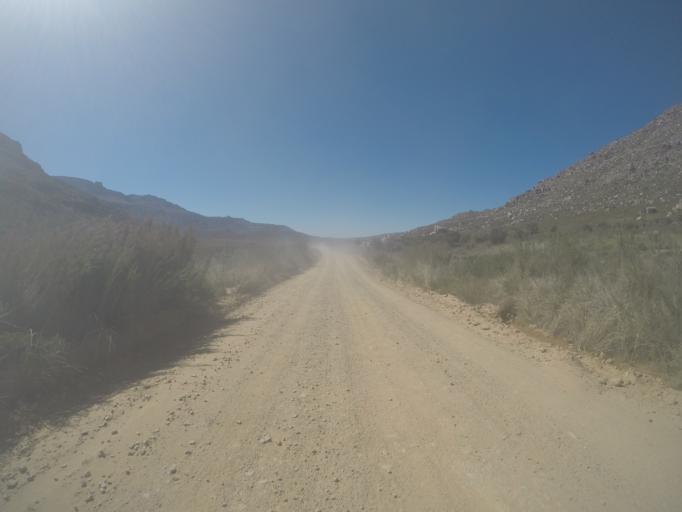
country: ZA
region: Western Cape
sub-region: West Coast District Municipality
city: Clanwilliam
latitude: -32.4300
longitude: 19.1415
